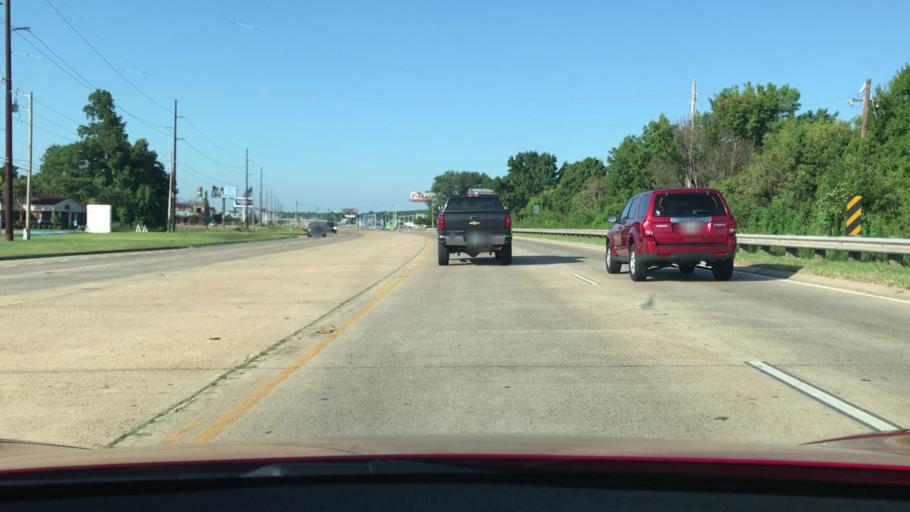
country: US
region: Louisiana
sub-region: Bossier Parish
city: Bossier City
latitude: 32.4261
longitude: -93.7189
